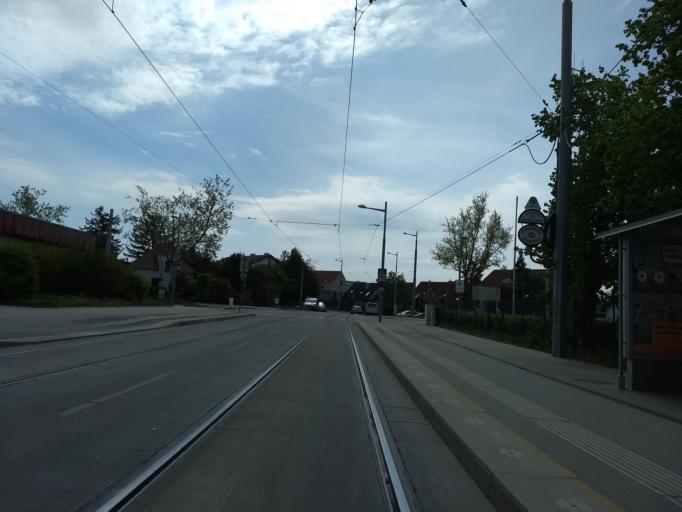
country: AT
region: Lower Austria
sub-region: Politischer Bezirk Wien-Umgebung
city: Gerasdorf bei Wien
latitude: 48.2392
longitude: 16.4842
